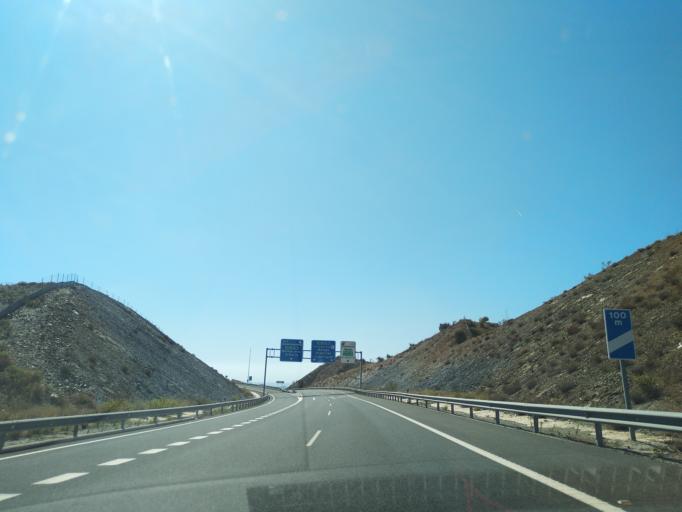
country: ES
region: Andalusia
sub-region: Provincia de Malaga
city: Malaga
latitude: 36.7625
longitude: -4.4885
